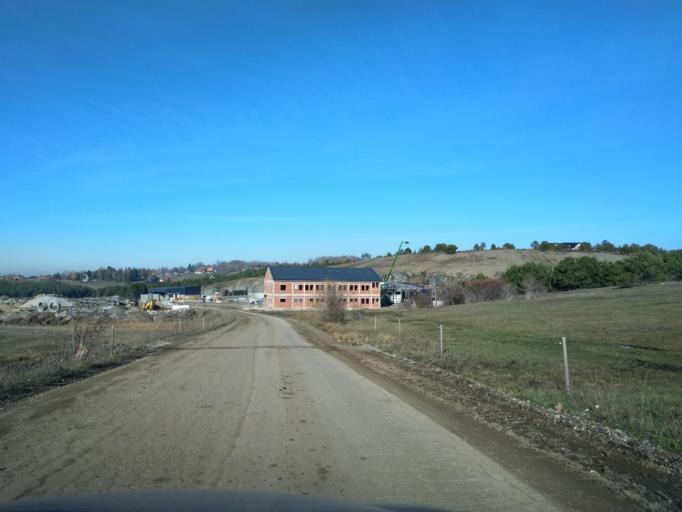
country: RS
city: Zlatibor
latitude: 43.7290
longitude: 19.6820
